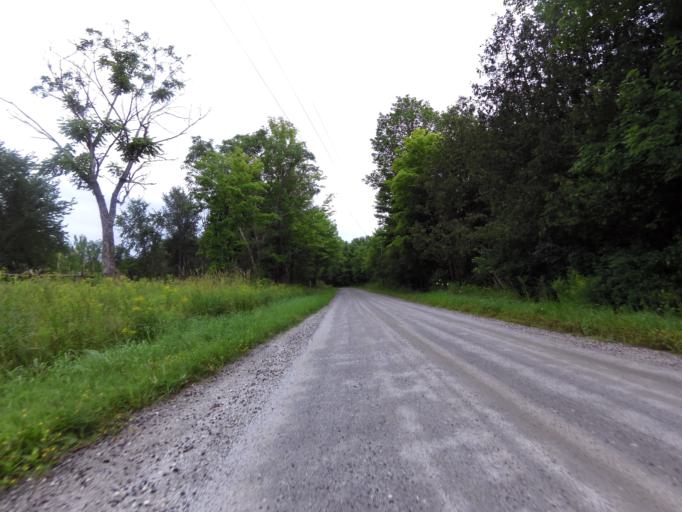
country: CA
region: Ontario
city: Perth
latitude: 45.0494
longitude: -76.3950
